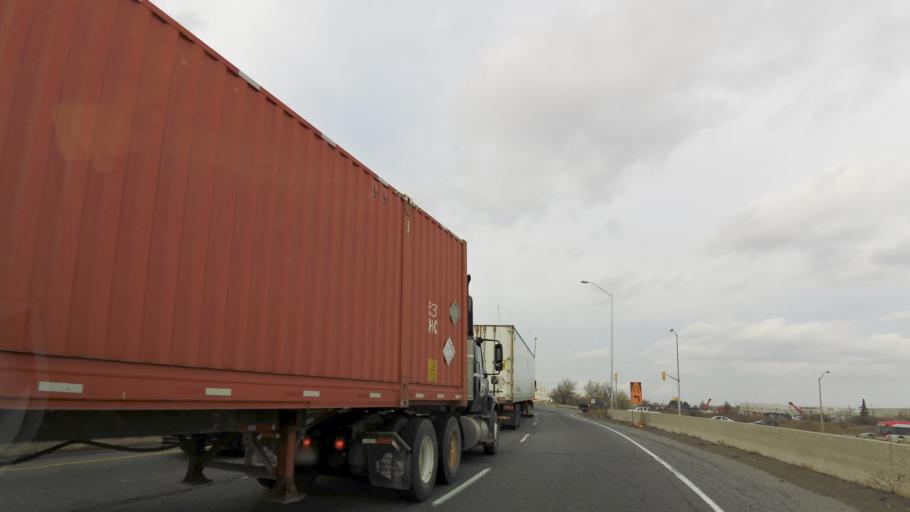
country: CA
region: Ontario
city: Etobicoke
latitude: 43.7338
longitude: -79.6253
